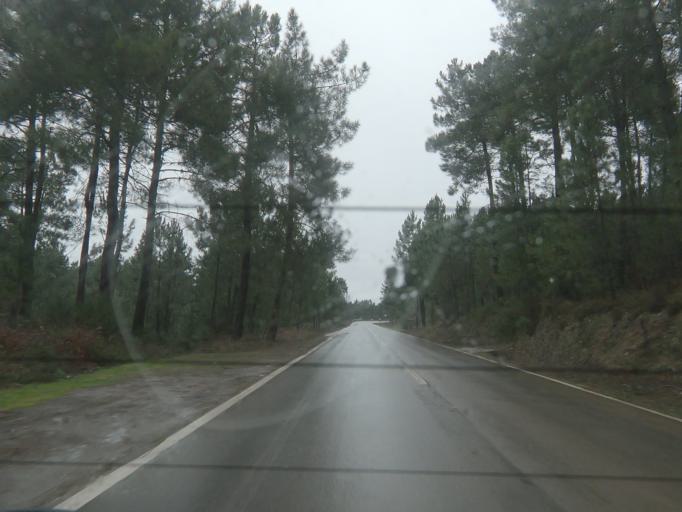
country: PT
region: Vila Real
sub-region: Sabrosa
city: Vilela
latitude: 41.2079
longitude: -7.6801
